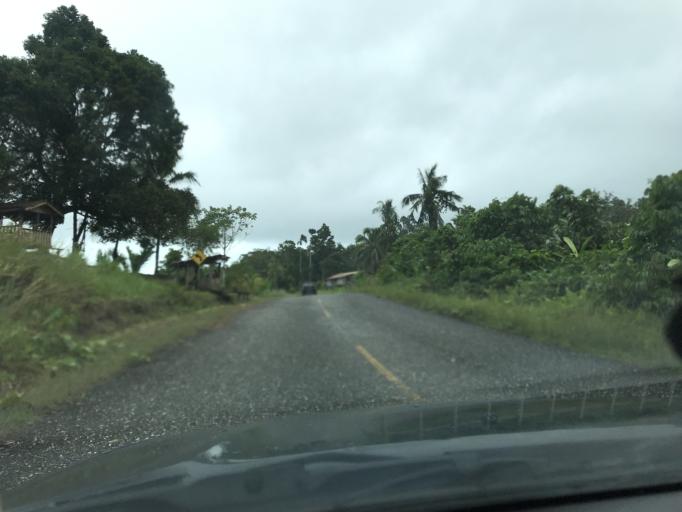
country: SB
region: Western Province
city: Gizo
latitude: -8.2461
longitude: 157.2356
